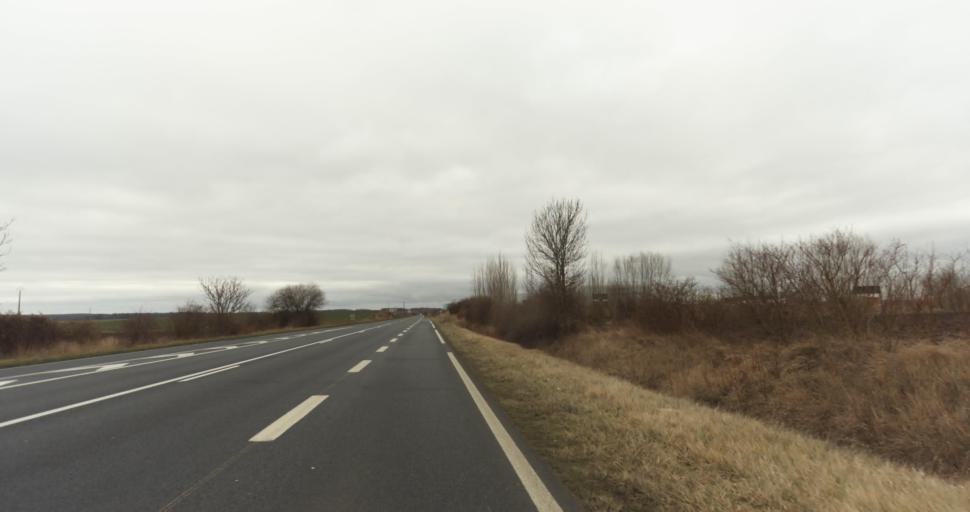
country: FR
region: Pays de la Loire
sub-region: Departement de Maine-et-Loire
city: Doue-la-Fontaine
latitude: 47.1947
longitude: -0.2446
